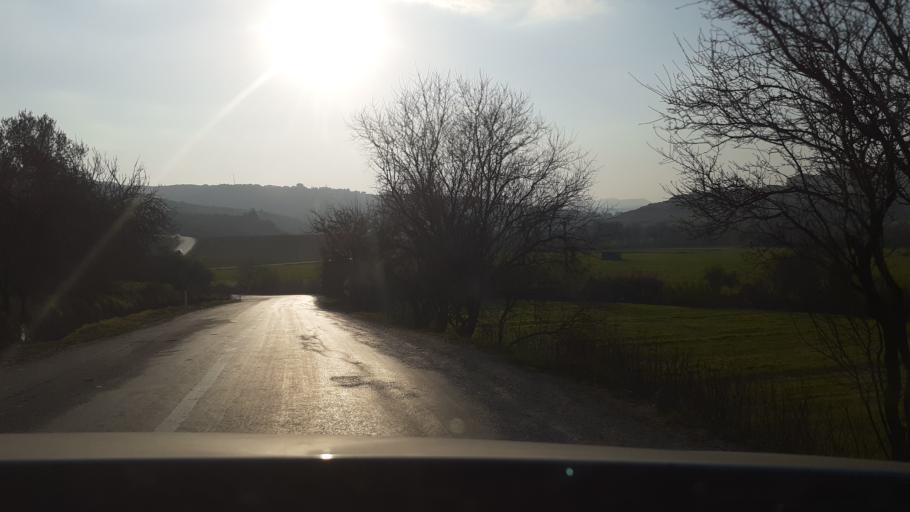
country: TR
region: Hatay
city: Oymakli
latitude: 36.1145
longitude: 36.2818
